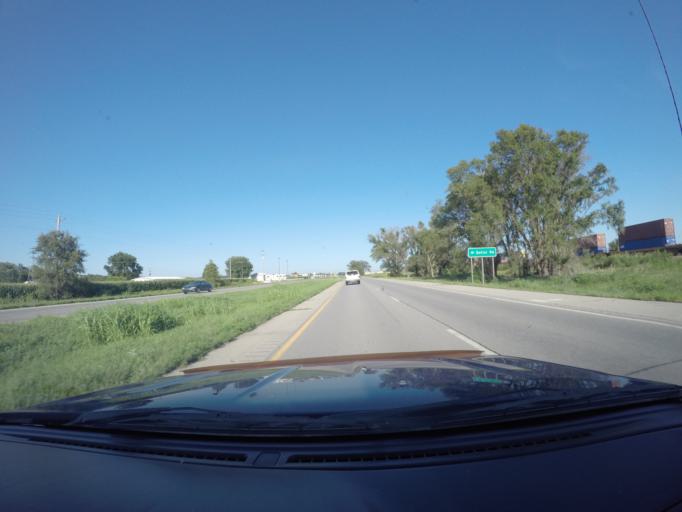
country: US
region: Kansas
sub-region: Shawnee County
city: Topeka
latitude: 39.0879
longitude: -95.5773
